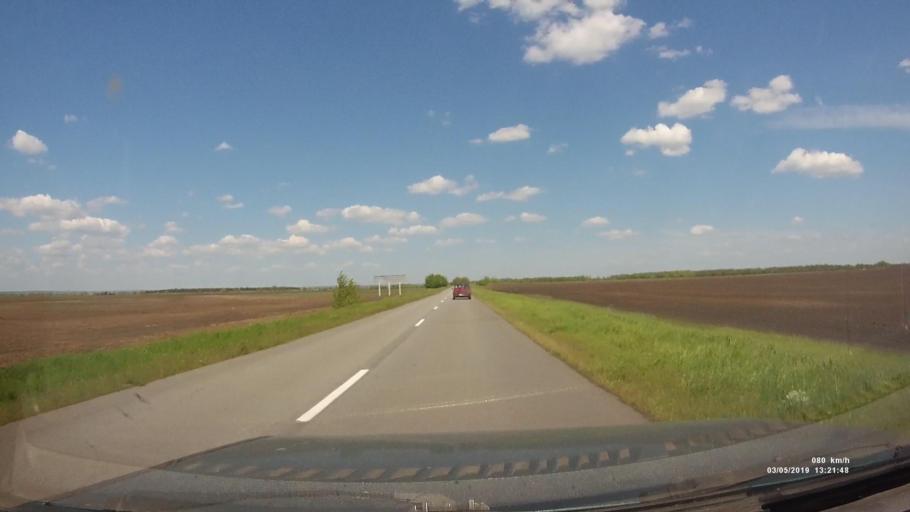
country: RU
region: Rostov
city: Semikarakorsk
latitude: 47.5575
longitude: 40.7501
